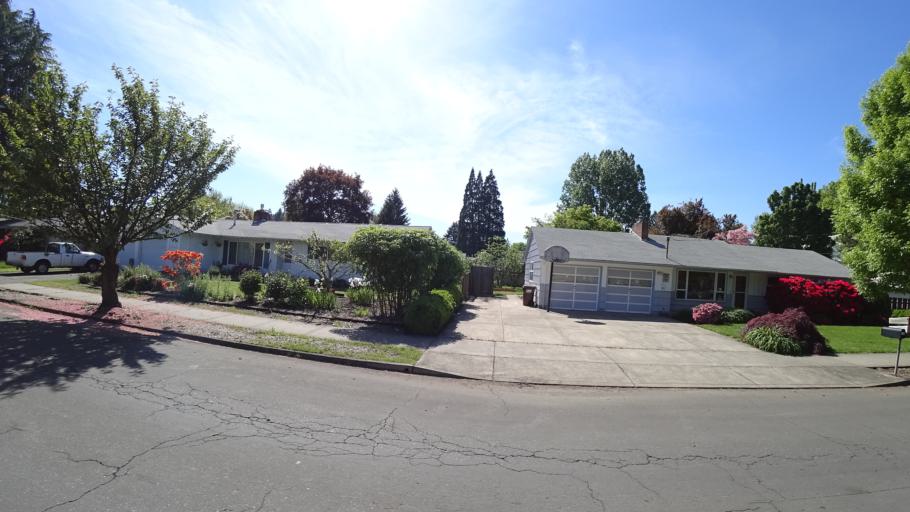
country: US
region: Oregon
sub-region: Washington County
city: Hillsboro
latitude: 45.5157
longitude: -122.9703
